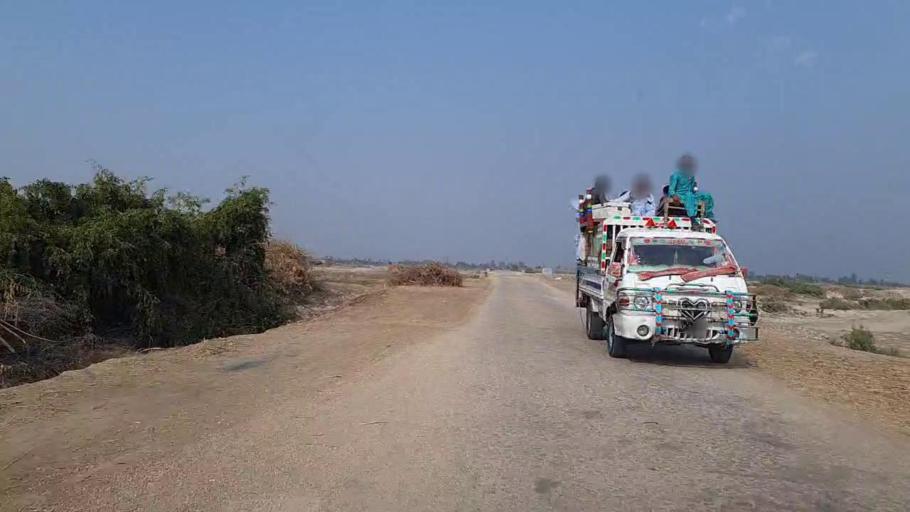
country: PK
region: Sindh
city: Mirwah Gorchani
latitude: 25.4152
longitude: 69.1454
